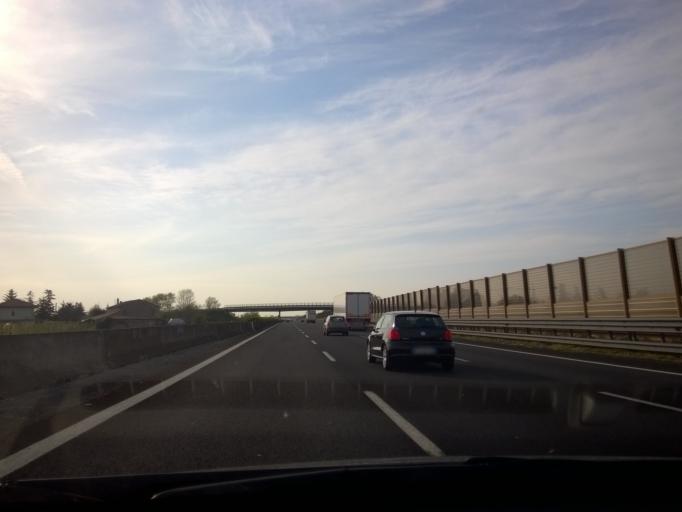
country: IT
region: Emilia-Romagna
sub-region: Forli-Cesena
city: Bagnarola
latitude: 44.1394
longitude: 12.3501
